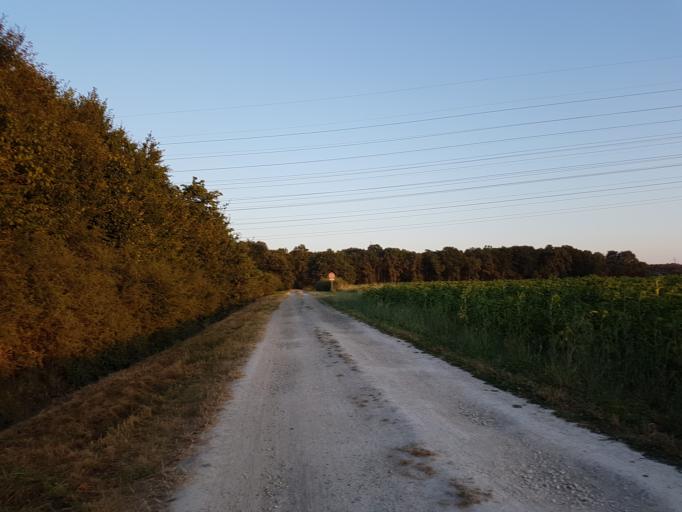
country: FR
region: Centre
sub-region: Departement d'Indre-et-Loire
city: Saint-Avertin
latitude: 47.3532
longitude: 0.7598
